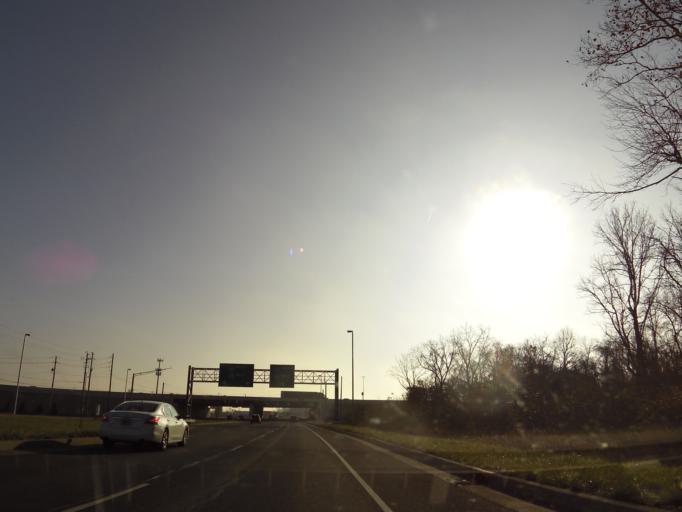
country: US
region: Indiana
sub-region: Marion County
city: Speedway
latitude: 39.8020
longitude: -86.2777
